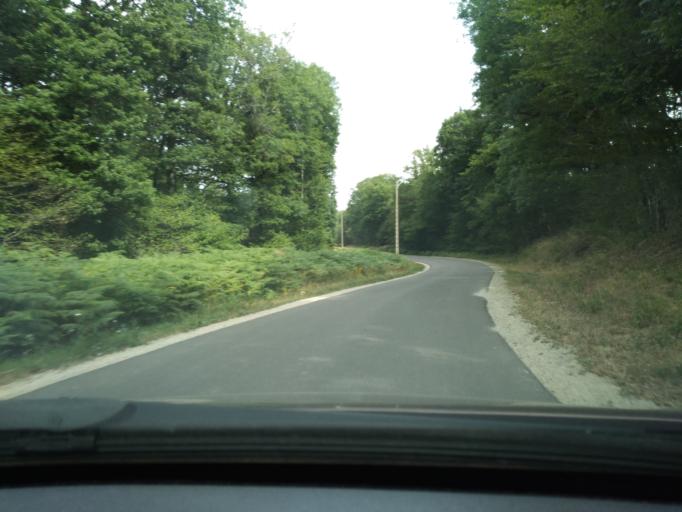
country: FR
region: Bourgogne
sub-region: Departement de la Cote-d'Or
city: Saulieu
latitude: 47.3758
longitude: 4.0795
